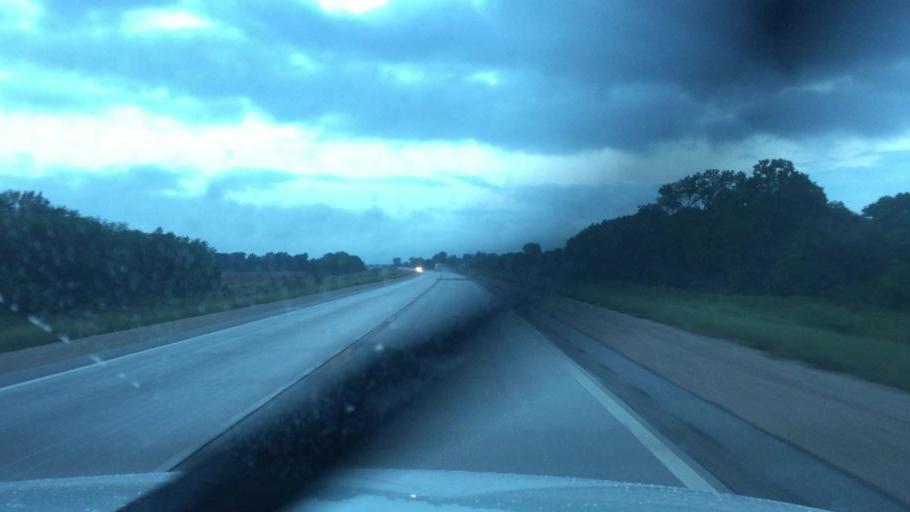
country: US
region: Kansas
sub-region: Neosho County
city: Chanute
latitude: 37.7377
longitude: -95.4502
